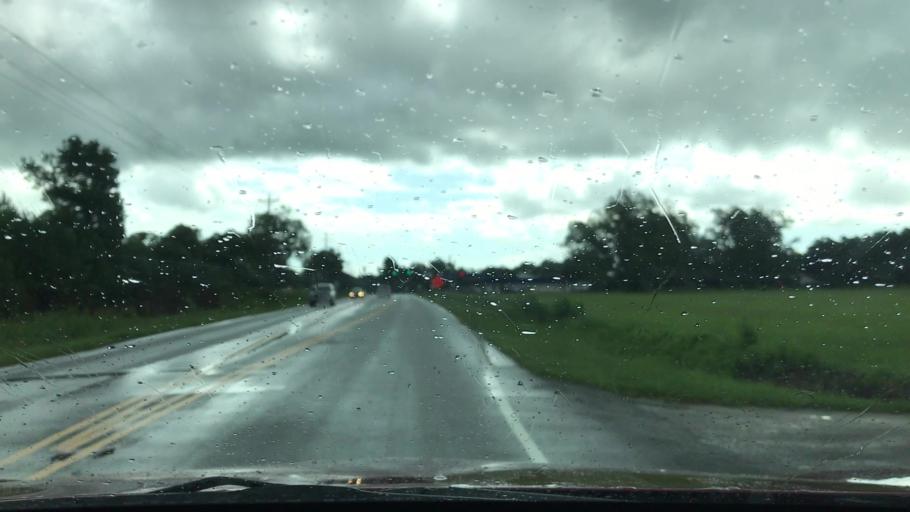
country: US
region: South Carolina
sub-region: Horry County
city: Loris
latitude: 33.9050
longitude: -78.8426
